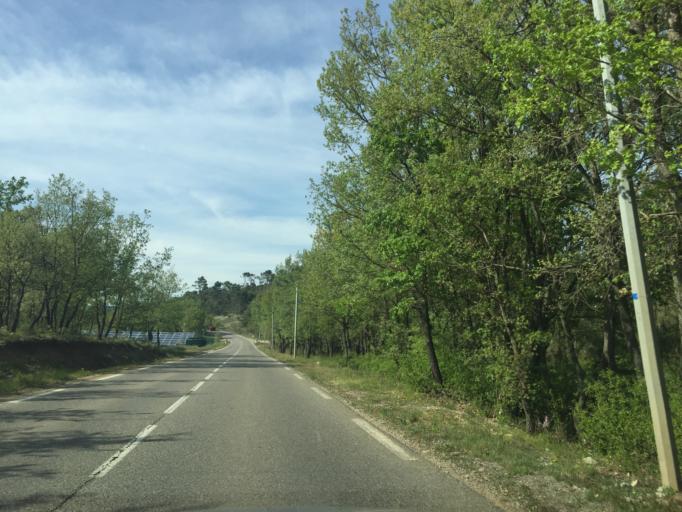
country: FR
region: Provence-Alpes-Cote d'Azur
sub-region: Departement du Var
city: Ginasservis
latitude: 43.6915
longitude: 5.8362
